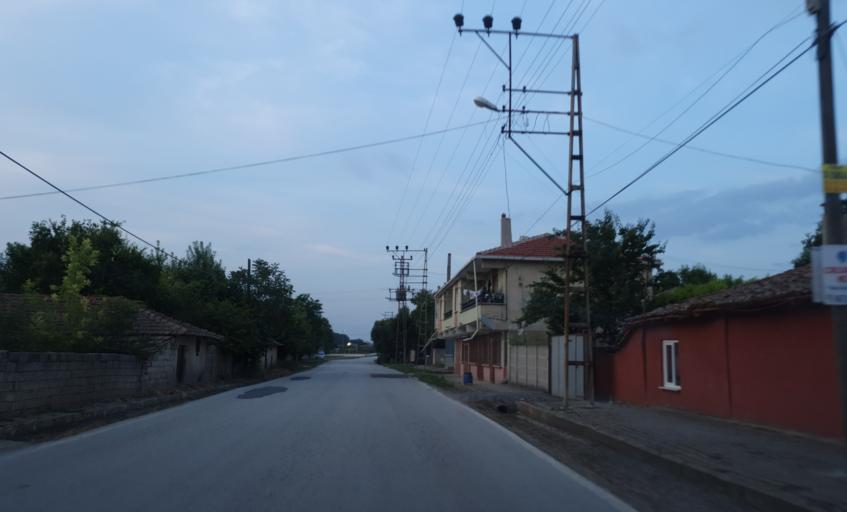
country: TR
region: Tekirdag
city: Beyazkoy
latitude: 41.3864
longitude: 27.6216
